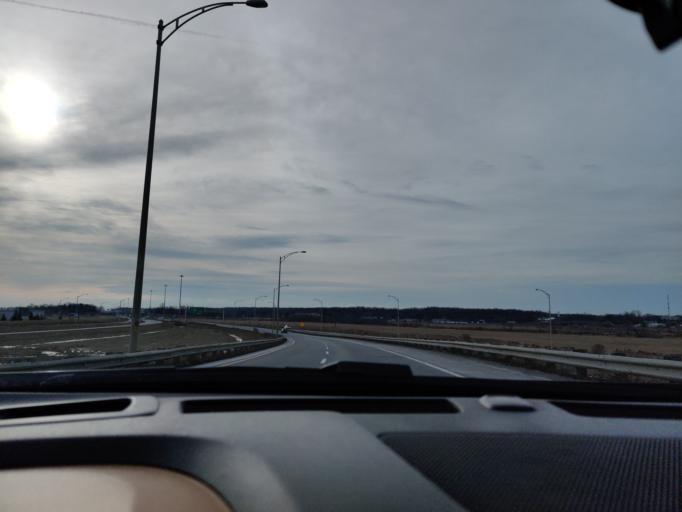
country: CA
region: Quebec
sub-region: Monteregie
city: Vaudreuil-Dorion
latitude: 45.3979
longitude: -74.0609
